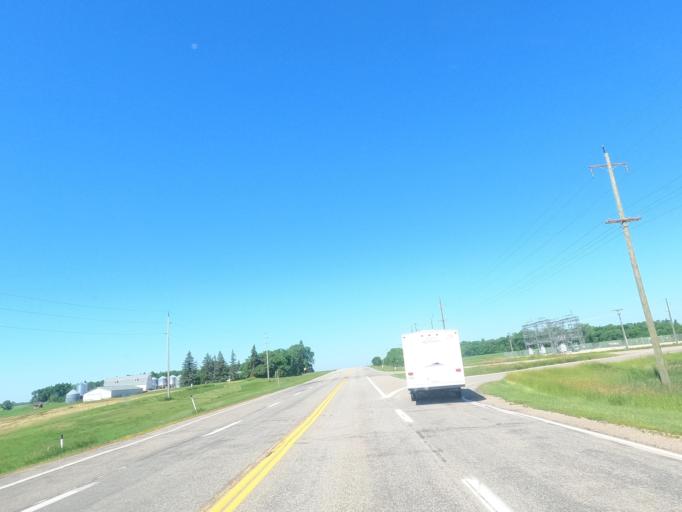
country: CA
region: Manitoba
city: Brandon
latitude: 49.5771
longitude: -99.6750
